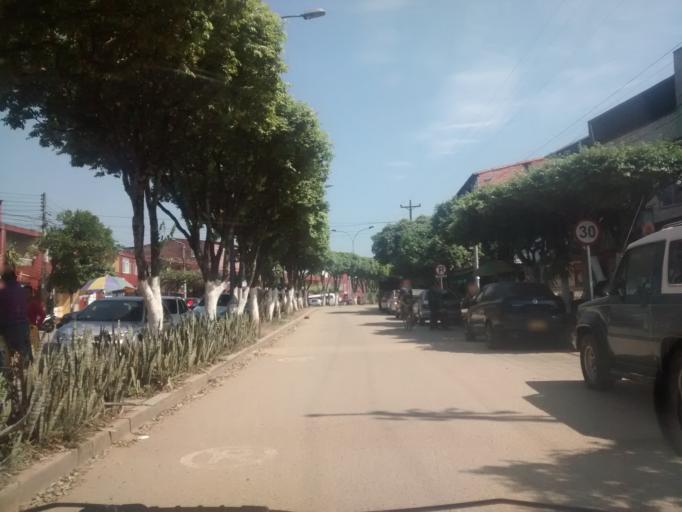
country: CO
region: Santander
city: Floridablanca
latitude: 7.0781
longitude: -73.1244
